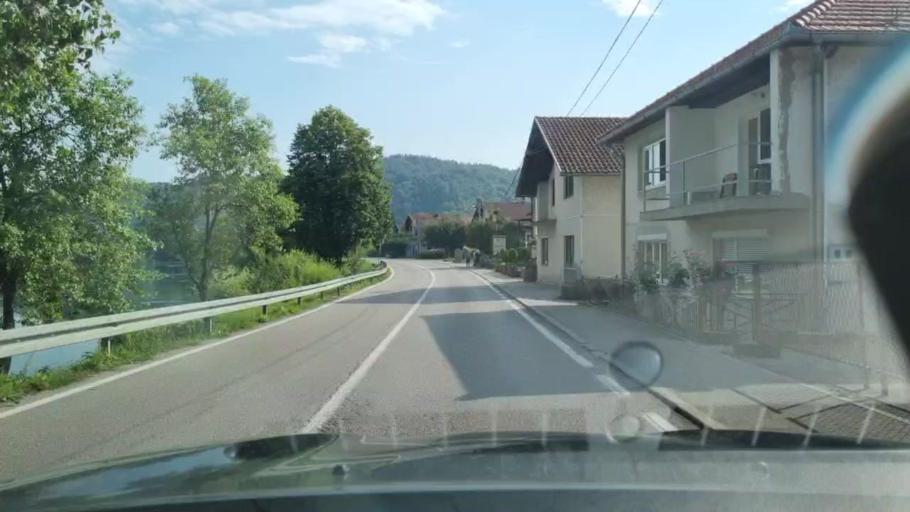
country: BA
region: Federation of Bosnia and Herzegovina
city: Otoka
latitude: 44.9589
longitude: 16.1826
